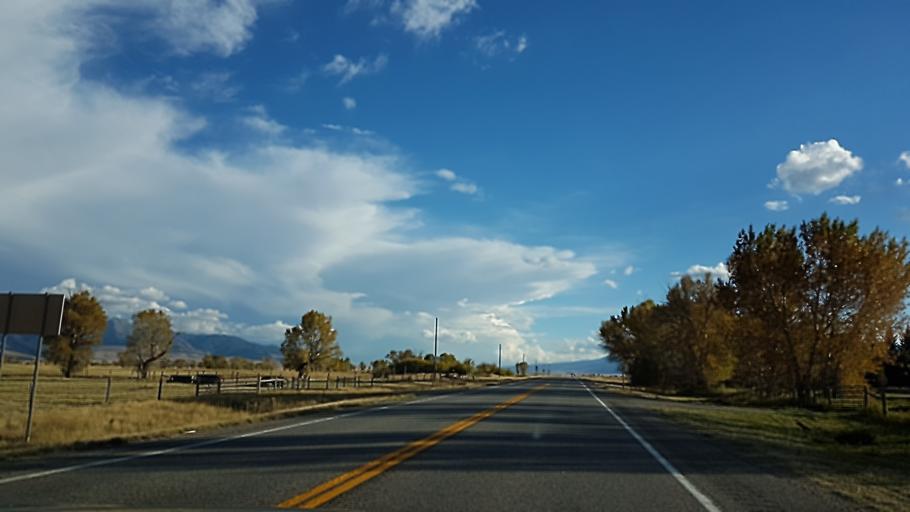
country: US
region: Montana
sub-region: Madison County
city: Virginia City
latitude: 45.2014
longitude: -111.6788
